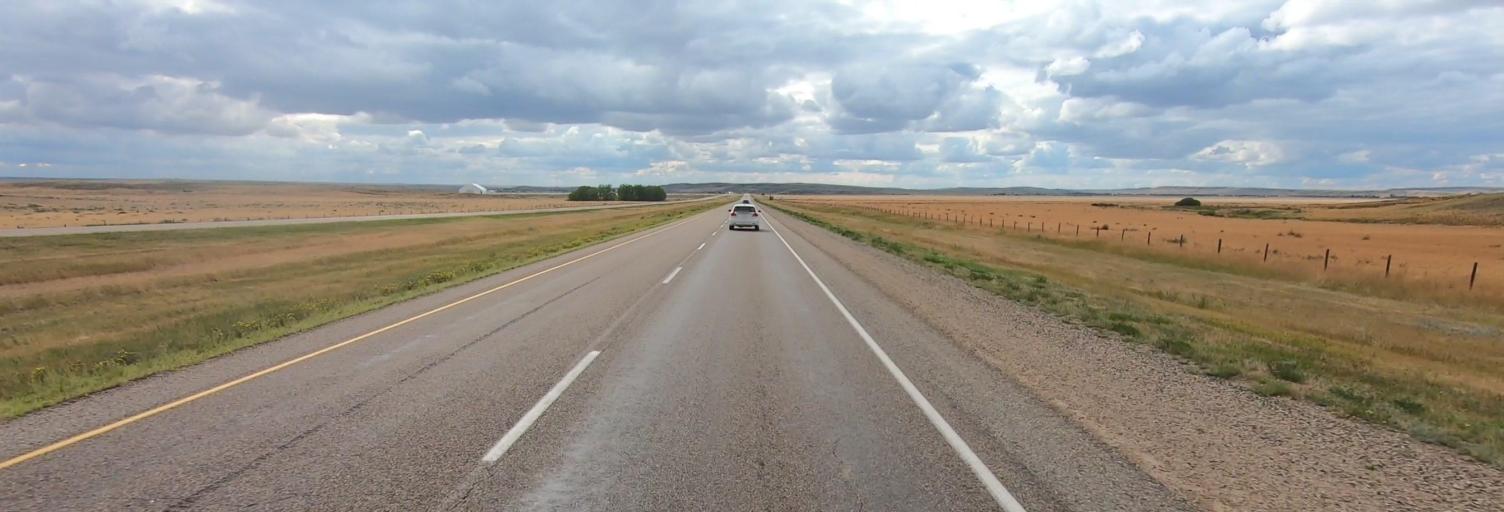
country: CA
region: Saskatchewan
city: Maple Creek
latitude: 49.9608
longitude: -109.9516
